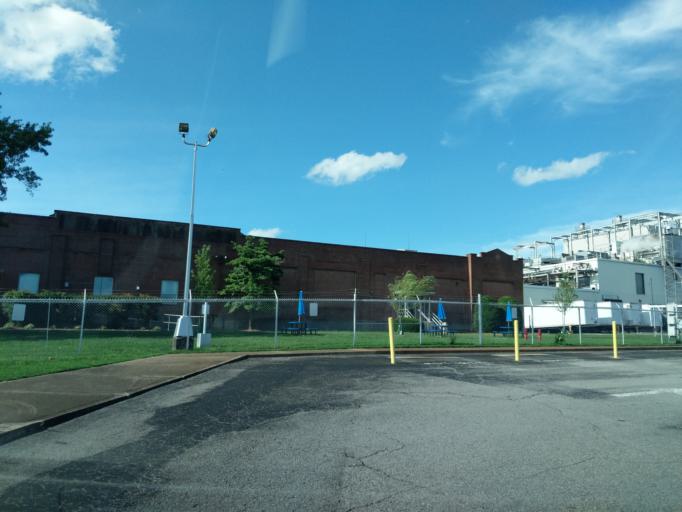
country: US
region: Tennessee
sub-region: Davidson County
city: Lakewood
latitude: 36.2683
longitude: -86.6550
